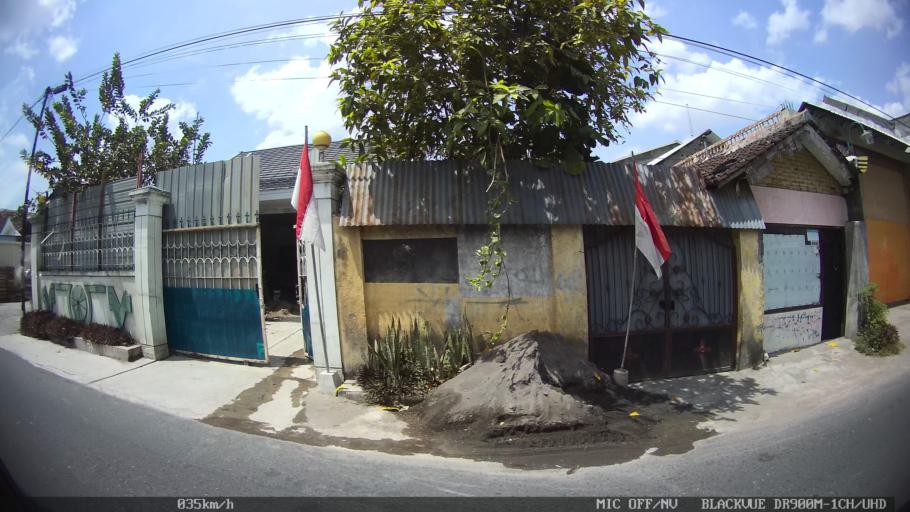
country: ID
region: Daerah Istimewa Yogyakarta
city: Gamping Lor
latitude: -7.8039
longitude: 110.3416
